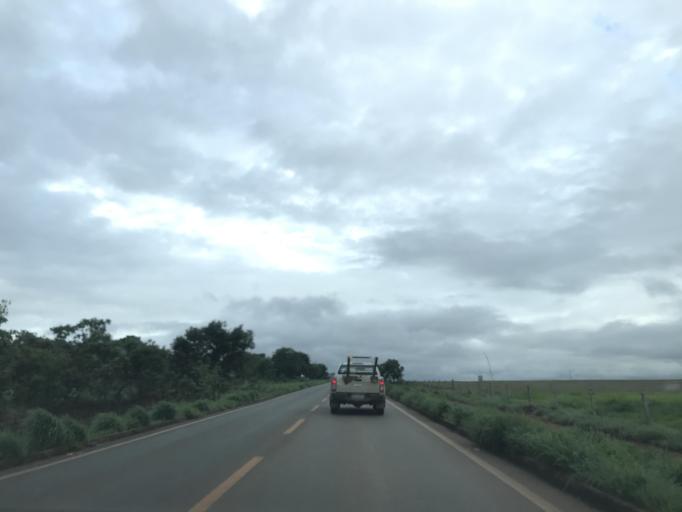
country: BR
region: Goias
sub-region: Luziania
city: Luziania
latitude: -16.2688
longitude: -47.9835
